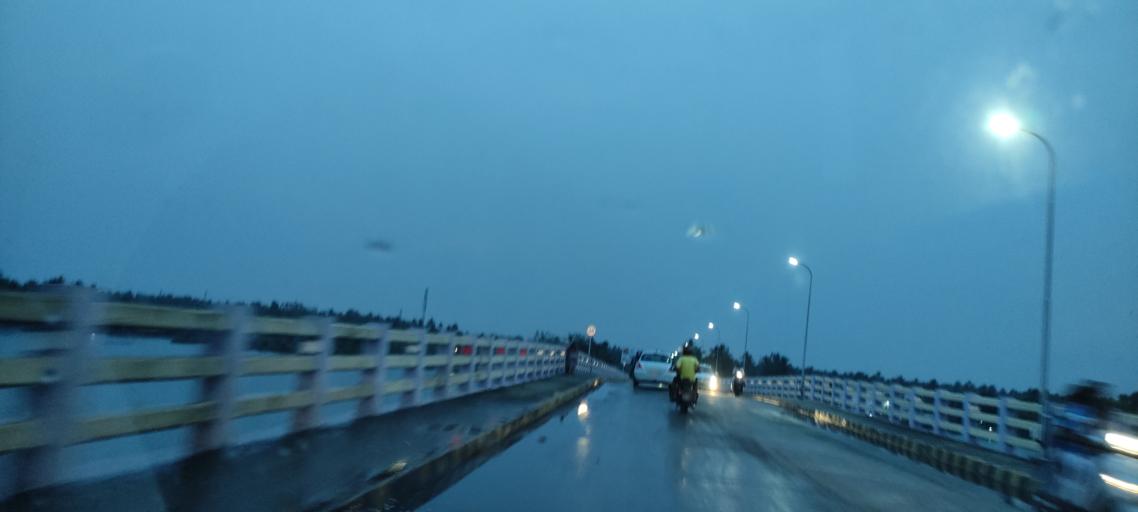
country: IN
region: Kerala
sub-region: Ernakulam
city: Cochin
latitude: 9.9242
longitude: 76.2877
